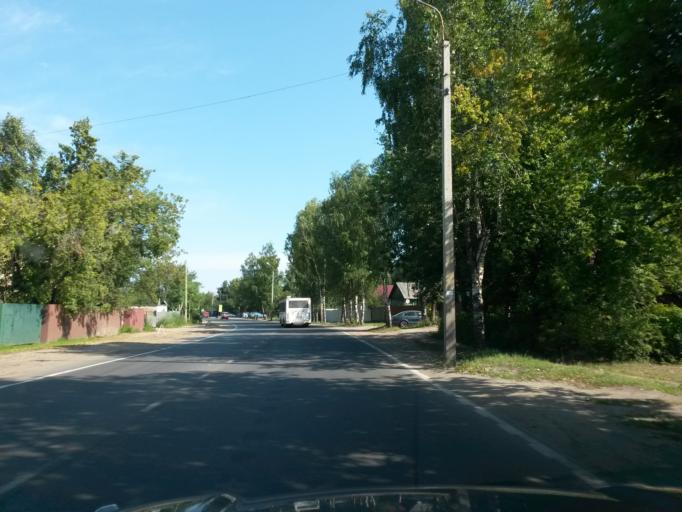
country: RU
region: Jaroslavl
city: Yaroslavl
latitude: 57.6581
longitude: 39.9100
